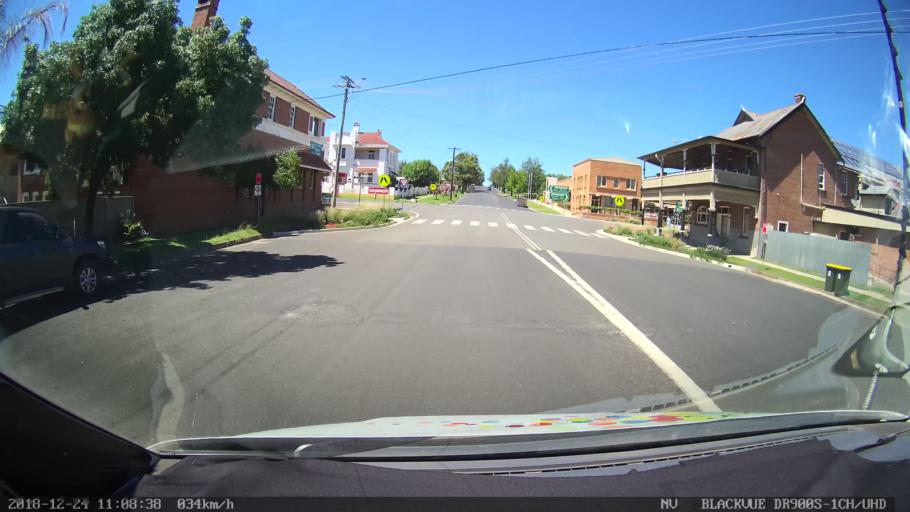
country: AU
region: New South Wales
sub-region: Upper Hunter Shire
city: Merriwa
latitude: -32.1389
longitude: 150.3558
